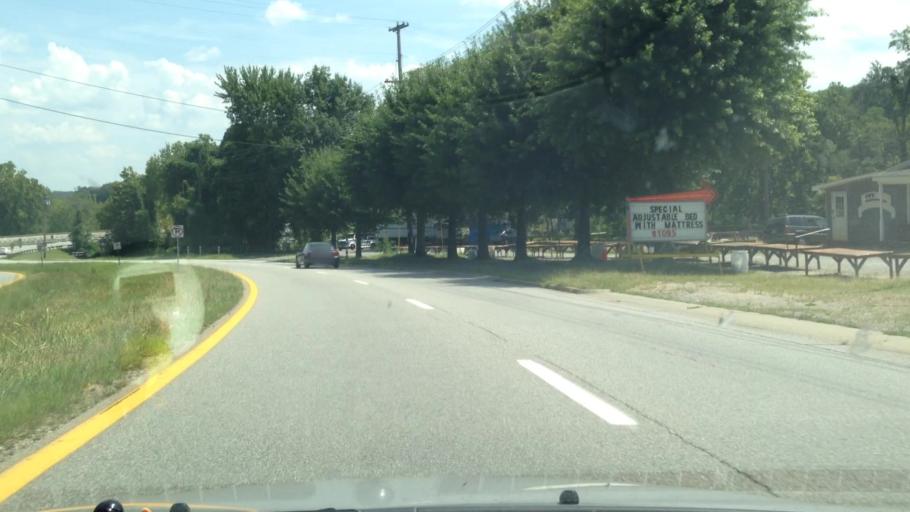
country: US
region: Virginia
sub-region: City of Martinsville
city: Martinsville
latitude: 36.6669
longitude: -79.8840
